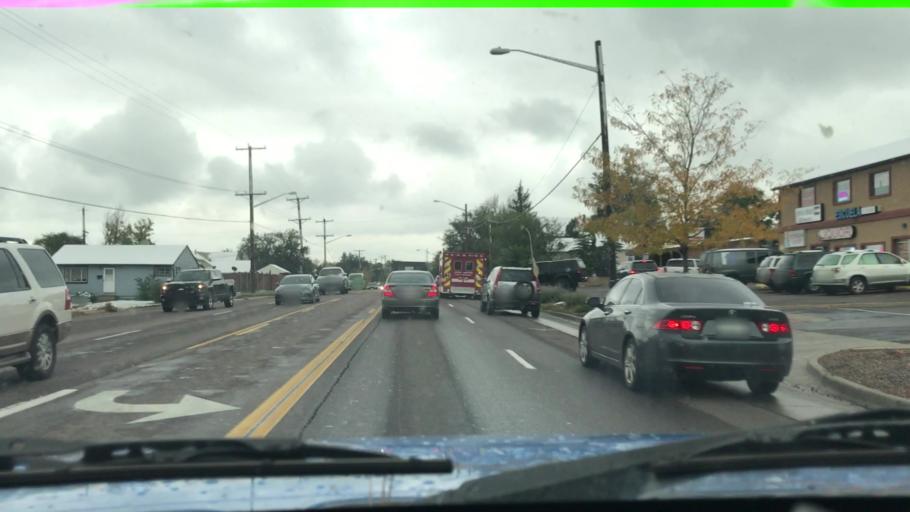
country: US
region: Colorado
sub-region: Jefferson County
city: Lakewood
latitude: 39.7108
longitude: -105.0533
